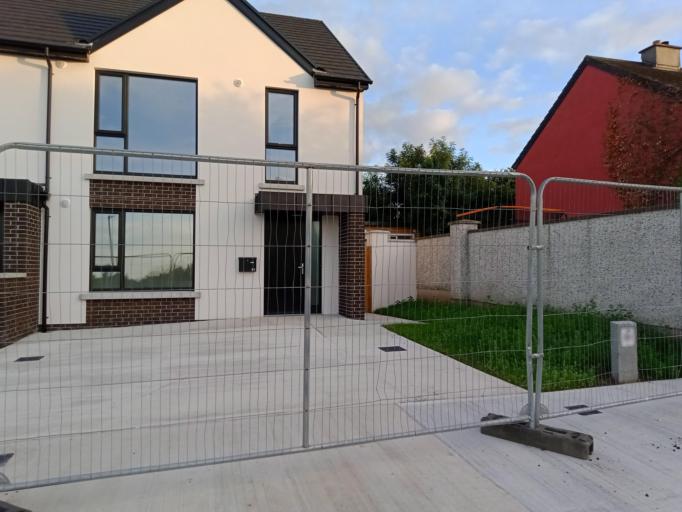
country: IE
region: Leinster
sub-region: Laois
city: Abbeyleix
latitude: 52.8399
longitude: -7.4032
